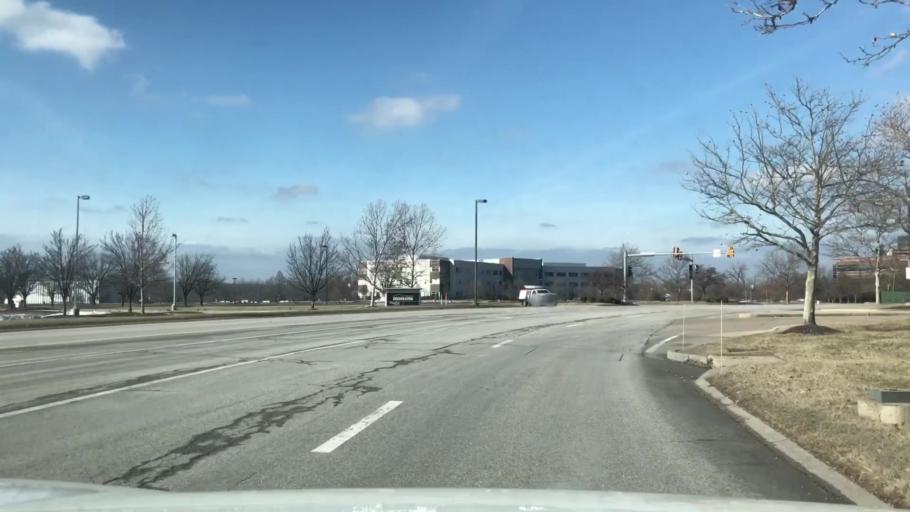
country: US
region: Missouri
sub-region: Saint Charles County
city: Saint Charles
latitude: 38.7495
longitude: -90.4640
